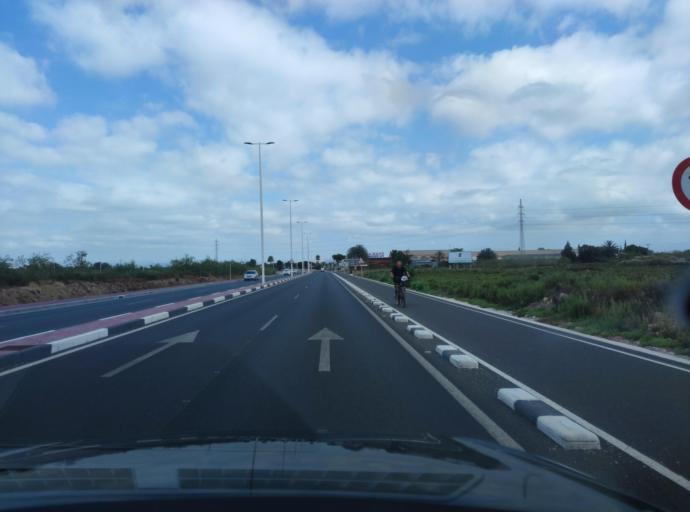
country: ES
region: Valencia
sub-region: Provincia de Alicante
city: Santa Pola
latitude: 38.2149
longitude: -0.5927
